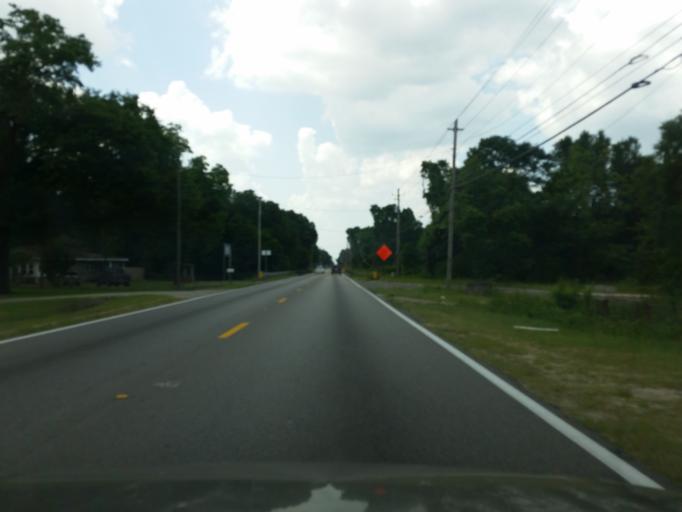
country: US
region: Florida
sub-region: Escambia County
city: Ensley
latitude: 30.5026
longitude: -87.2579
